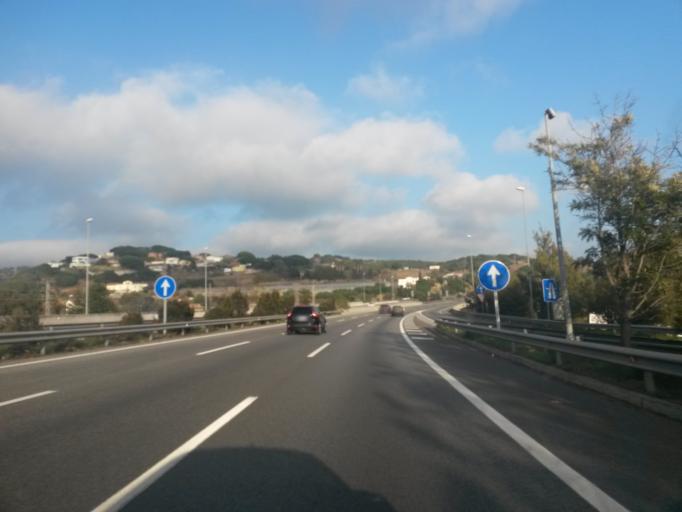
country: ES
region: Catalonia
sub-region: Provincia de Barcelona
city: Arenys de Mar
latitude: 41.5903
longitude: 2.5414
